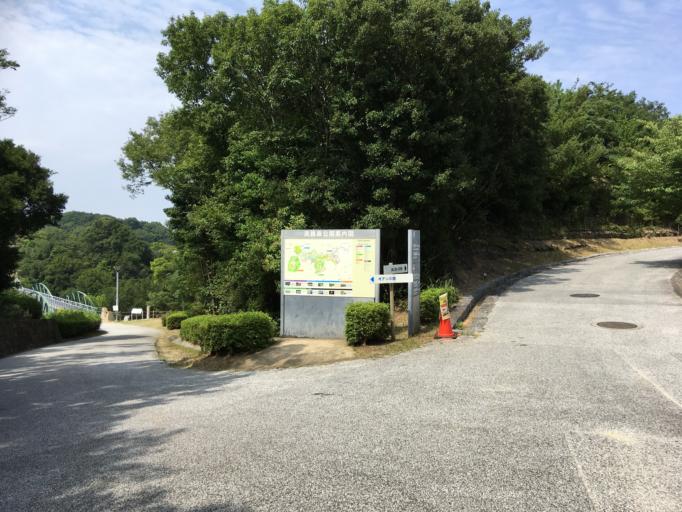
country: JP
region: Hyogo
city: Akashi
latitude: 34.5745
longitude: 135.0059
